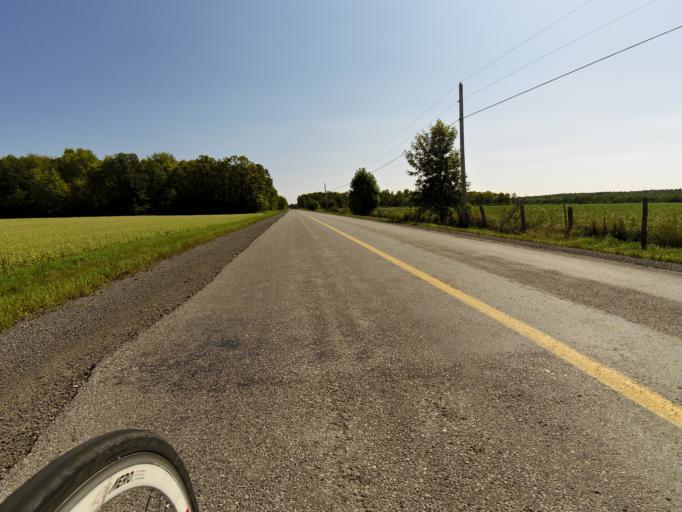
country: CA
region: Ontario
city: Bells Corners
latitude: 45.4365
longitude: -76.0654
